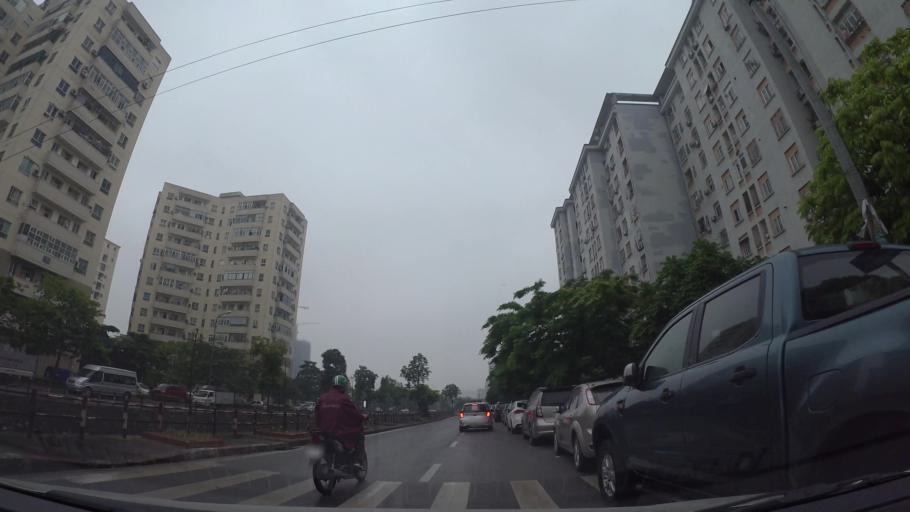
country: VN
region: Ha Noi
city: Cau Giay
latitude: 21.0158
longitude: 105.7872
